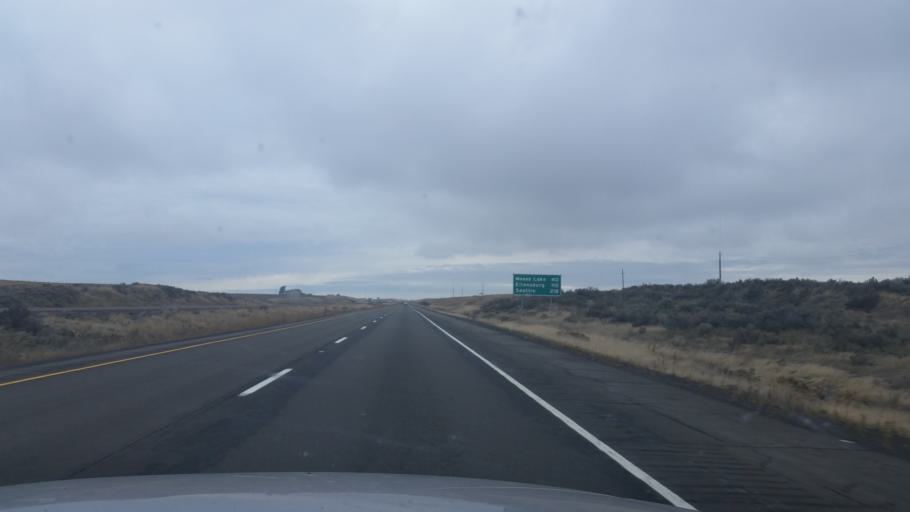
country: US
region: Washington
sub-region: Adams County
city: Ritzville
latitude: 47.1113
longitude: -118.4135
